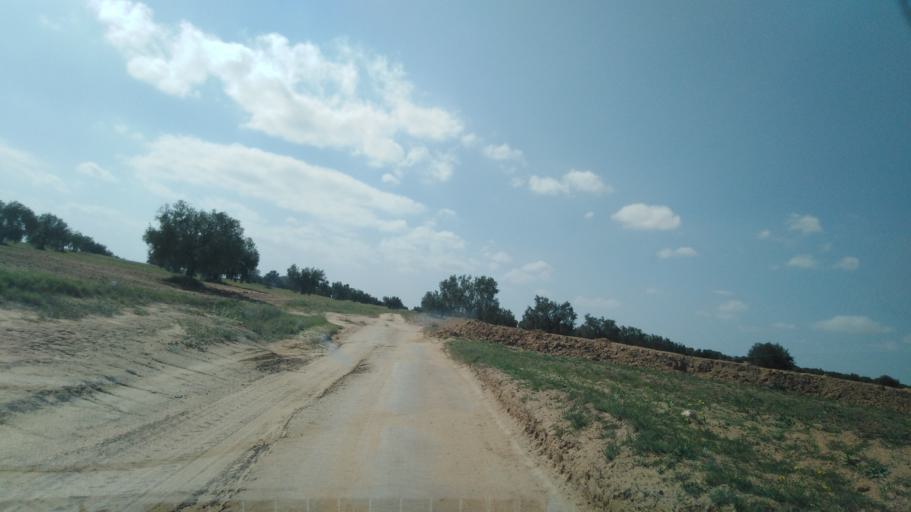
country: TN
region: Safaqis
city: Bi'r `Ali Bin Khalifah
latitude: 34.7921
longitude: 10.4006
